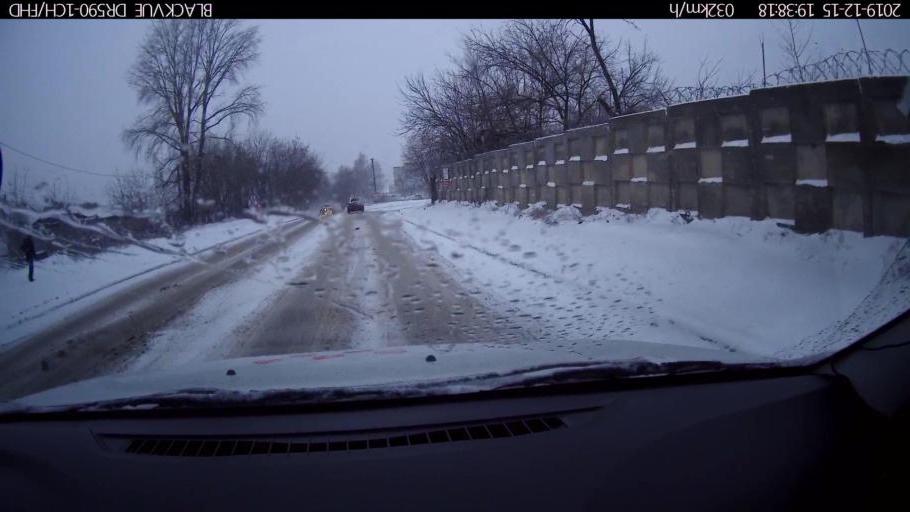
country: RU
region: Nizjnij Novgorod
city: Bor
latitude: 56.3075
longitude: 44.0540
